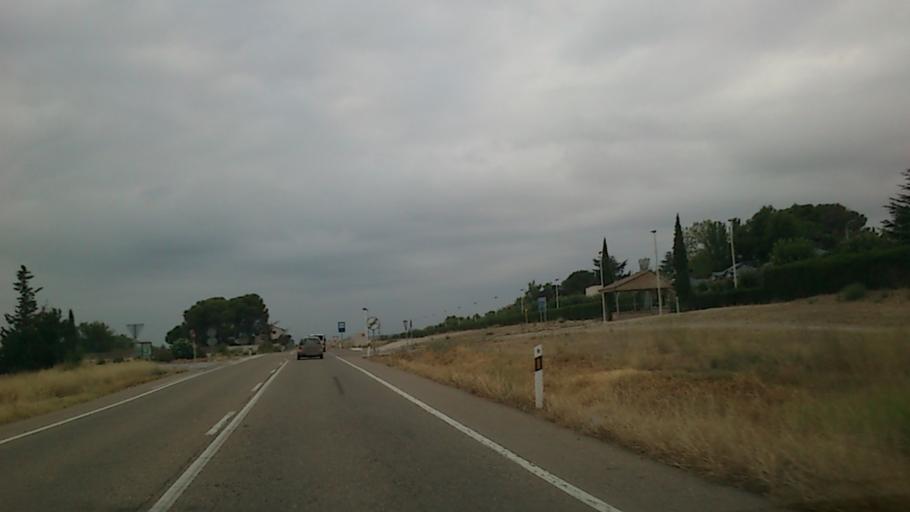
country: ES
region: Aragon
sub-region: Provincia de Zaragoza
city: Villanueva de Gallego
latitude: 41.7992
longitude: -0.8103
